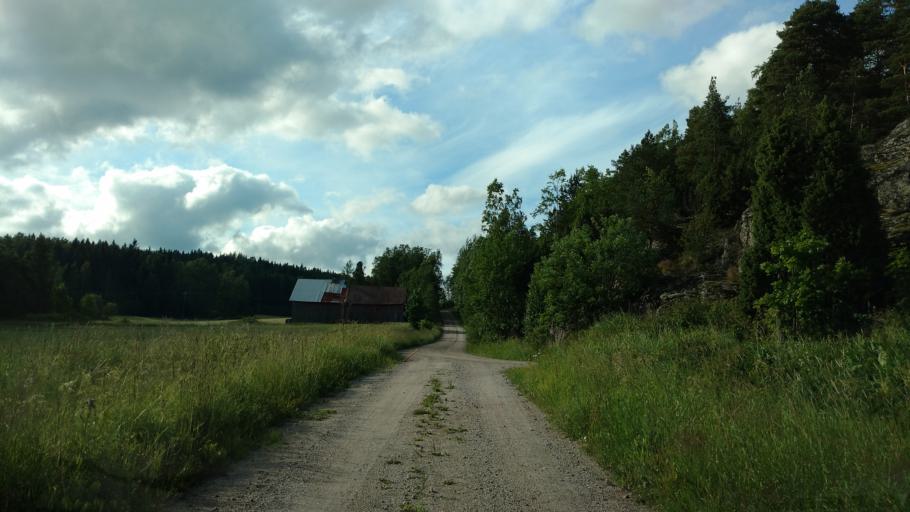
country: FI
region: Varsinais-Suomi
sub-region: Salo
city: Salo
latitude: 60.4255
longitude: 23.1756
